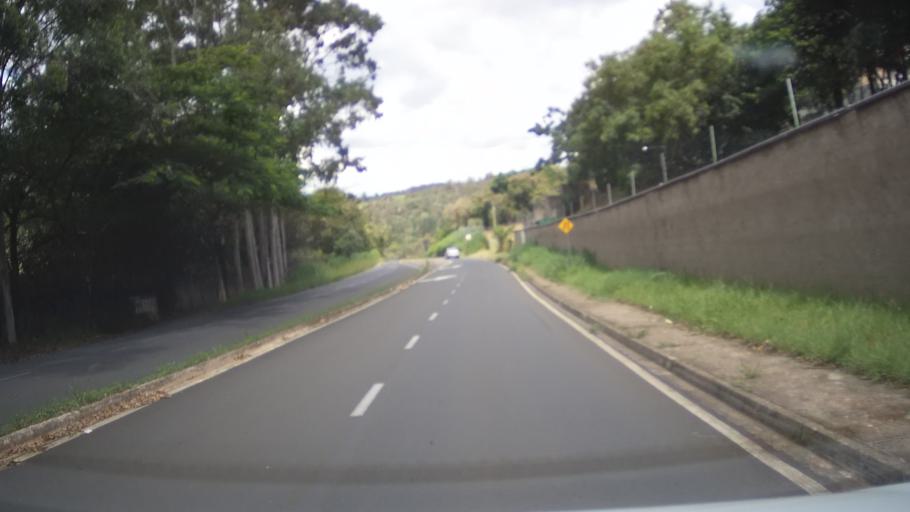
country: BR
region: Sao Paulo
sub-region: Valinhos
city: Valinhos
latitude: -22.9768
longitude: -46.9682
